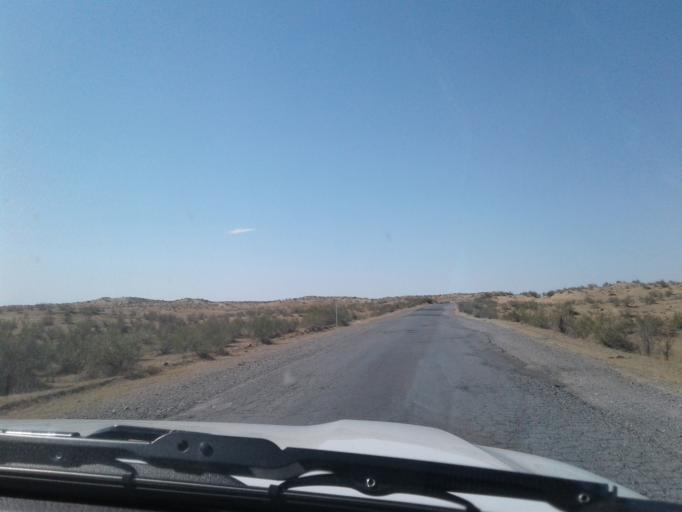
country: AF
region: Badghis
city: Bala Murghab
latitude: 36.2456
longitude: 62.5966
